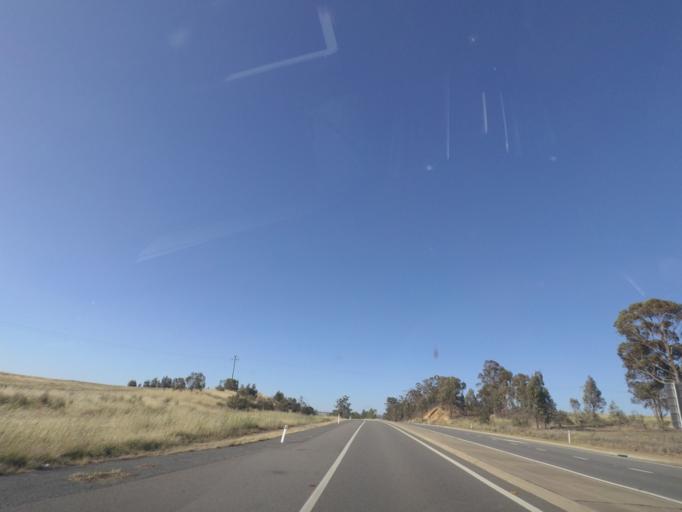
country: AU
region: New South Wales
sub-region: Wagga Wagga
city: Forest Hill
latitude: -35.2670
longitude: 147.7459
